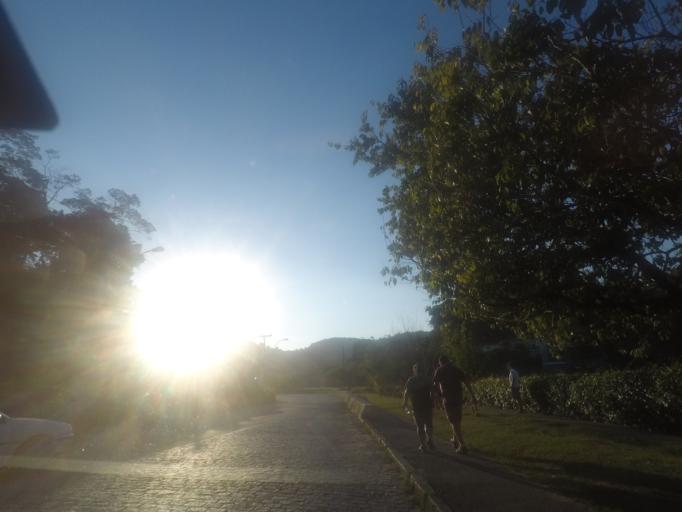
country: BR
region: Rio de Janeiro
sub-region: Petropolis
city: Petropolis
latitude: -22.5297
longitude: -43.2129
